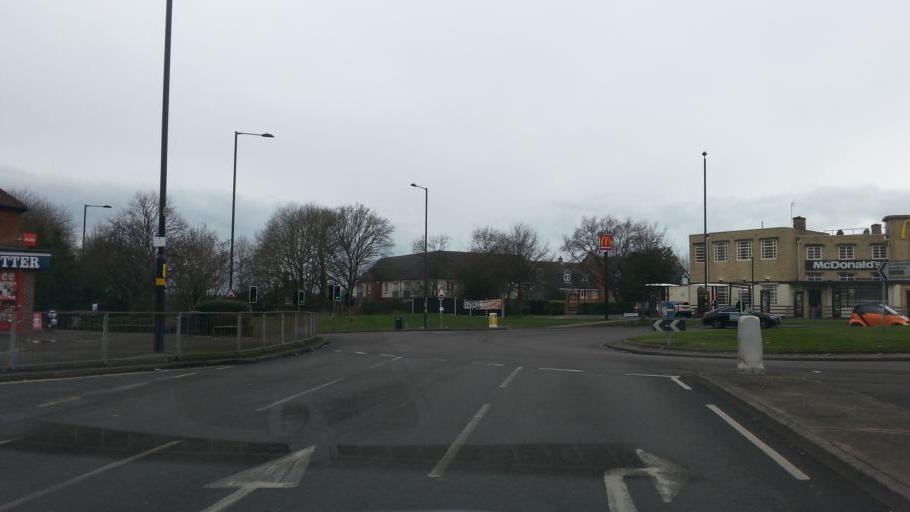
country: GB
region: England
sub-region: Solihull
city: Tidbury Green
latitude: 52.4082
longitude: -1.9162
